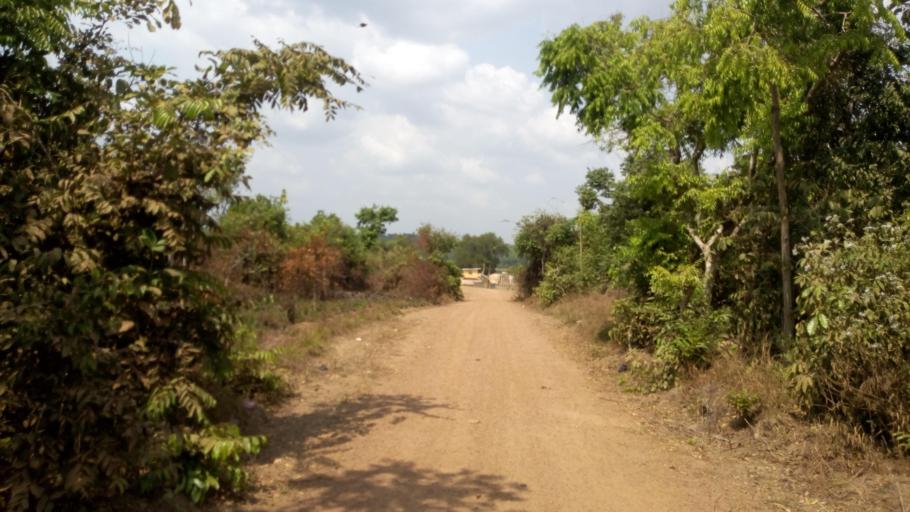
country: SL
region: Southern Province
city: Mogbwemo
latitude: 7.7944
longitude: -12.3075
